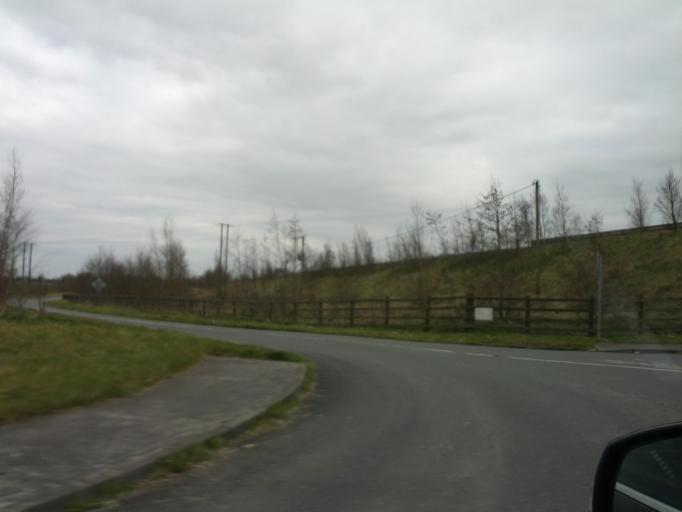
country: IE
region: Connaught
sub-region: County Galway
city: Athenry
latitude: 53.2819
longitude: -8.7436
